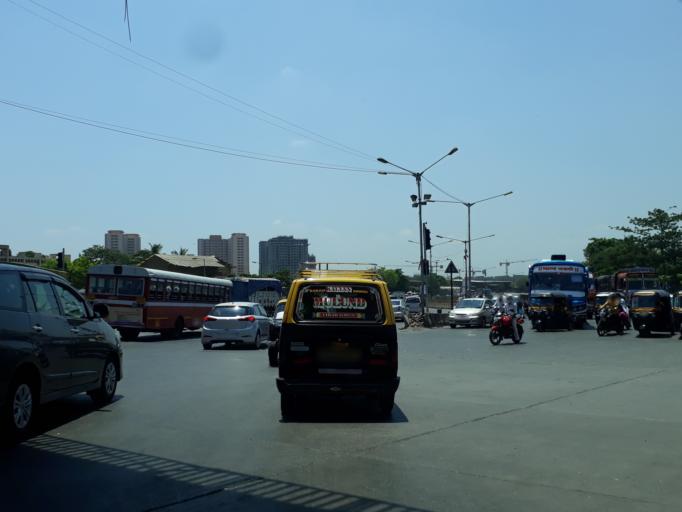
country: IN
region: Maharashtra
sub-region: Mumbai Suburban
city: Mumbai
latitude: 19.0707
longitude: 72.9071
